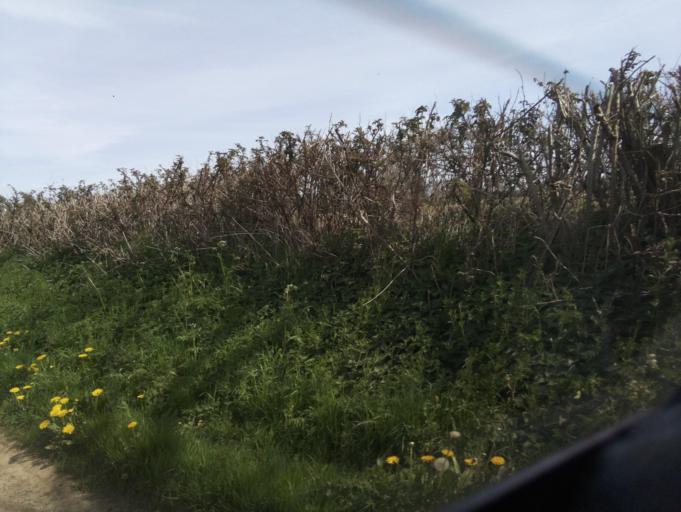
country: GB
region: England
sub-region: Dorset
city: Sherborne
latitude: 50.9931
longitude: -2.5440
